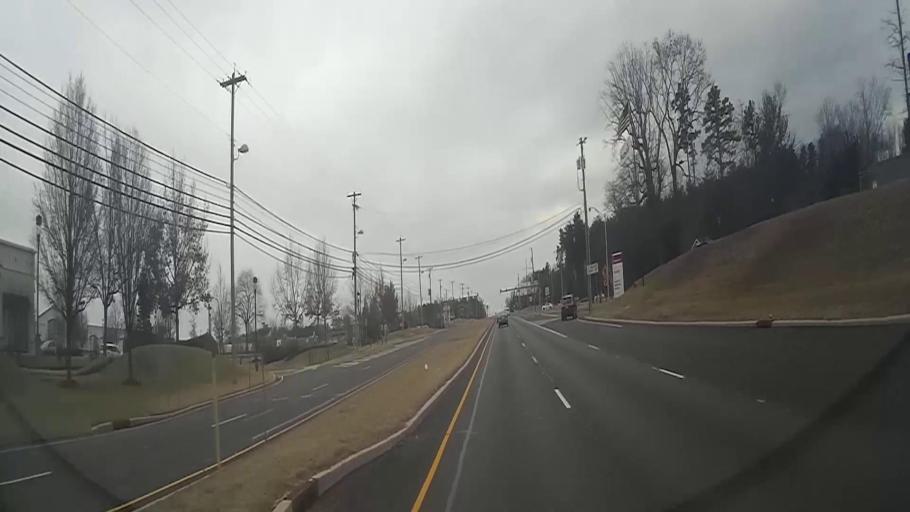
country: US
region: New Jersey
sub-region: Camden County
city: Gibbsboro
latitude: 39.8375
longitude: -74.9254
